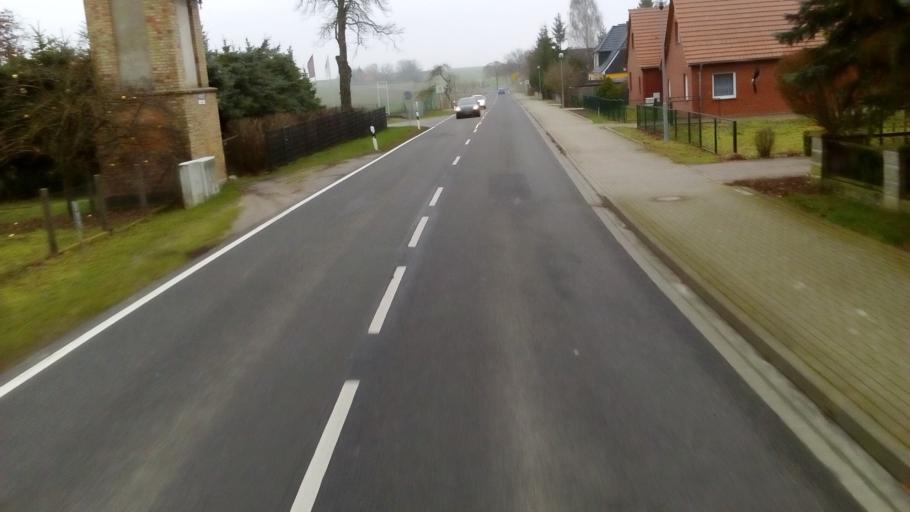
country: DE
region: Mecklenburg-Vorpommern
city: Strasburg
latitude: 53.4920
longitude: 13.8057
